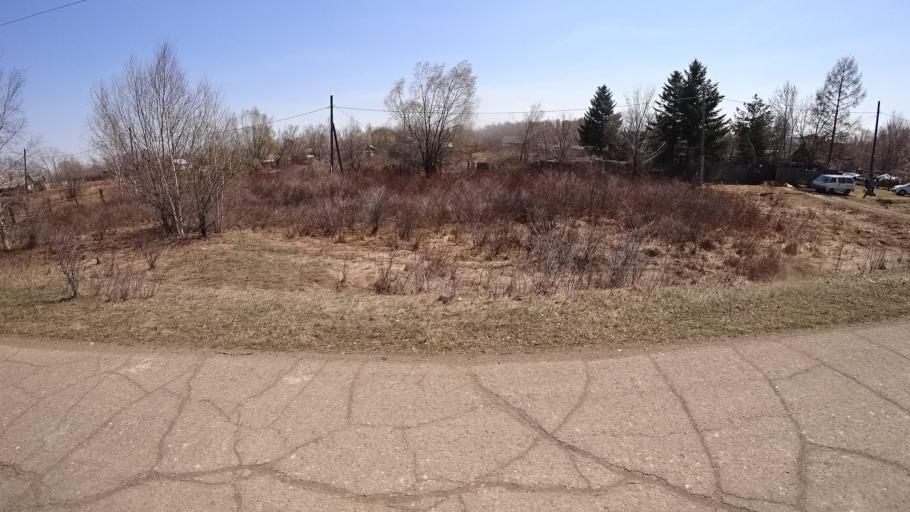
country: RU
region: Khabarovsk Krai
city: Khurba
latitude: 50.4063
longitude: 136.8735
